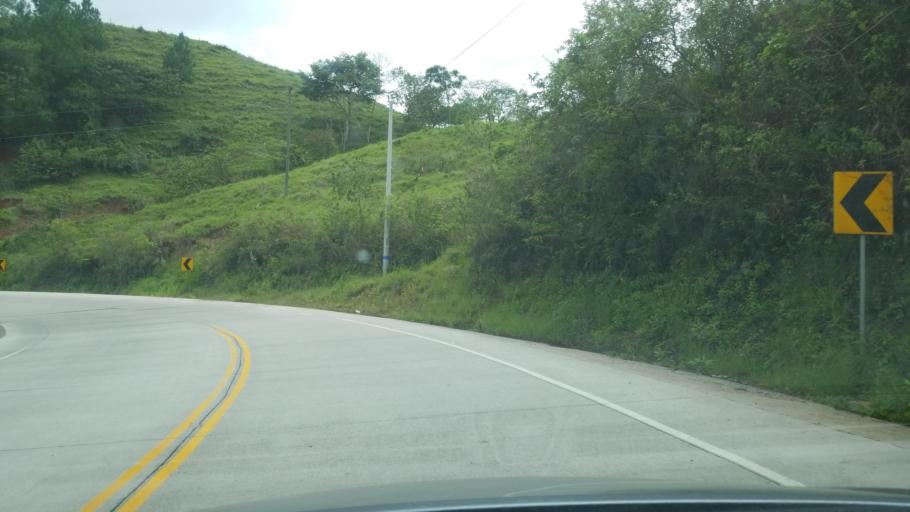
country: HN
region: Copan
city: San Jeronimo
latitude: 14.9324
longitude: -88.9509
